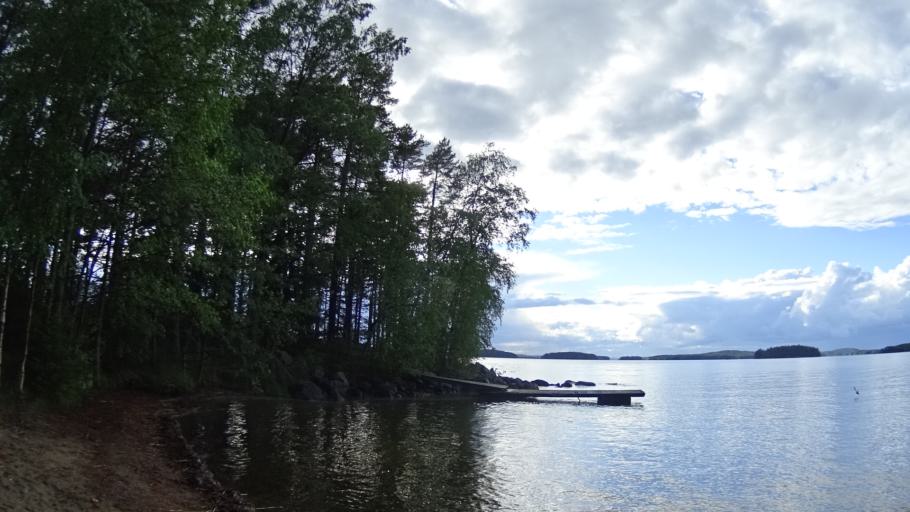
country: FI
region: Paijanne Tavastia
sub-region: Lahti
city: Sysmae
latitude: 61.4827
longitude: 25.5613
